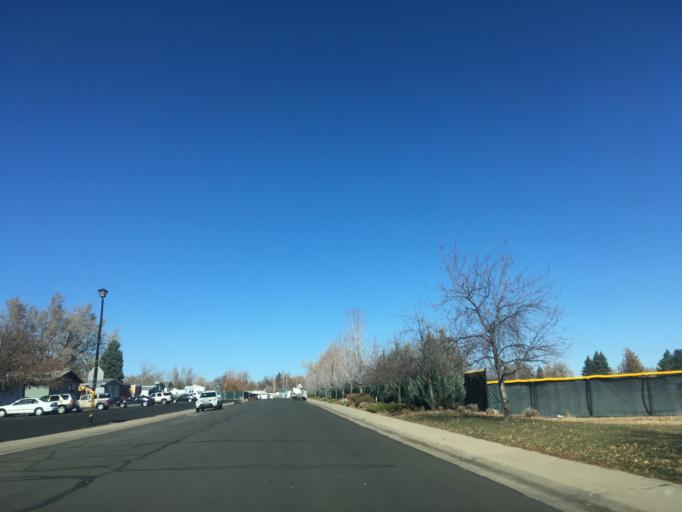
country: US
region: Colorado
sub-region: Boulder County
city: Lafayette
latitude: 39.9919
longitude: -105.0811
